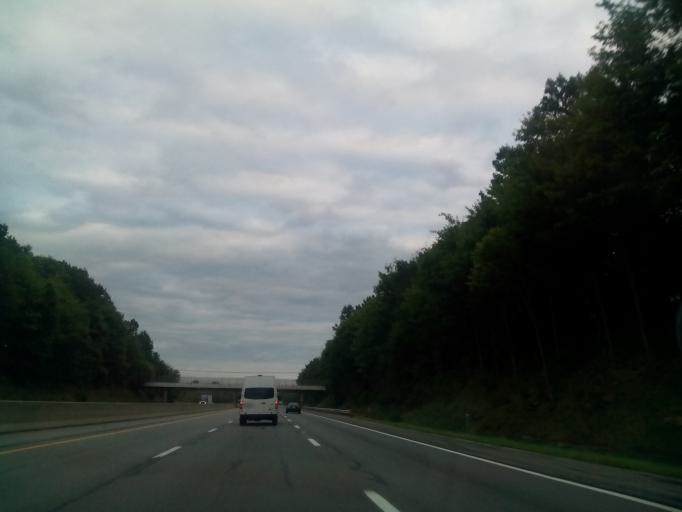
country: US
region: Ohio
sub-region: Portage County
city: Windham
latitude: 41.2416
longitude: -81.0325
